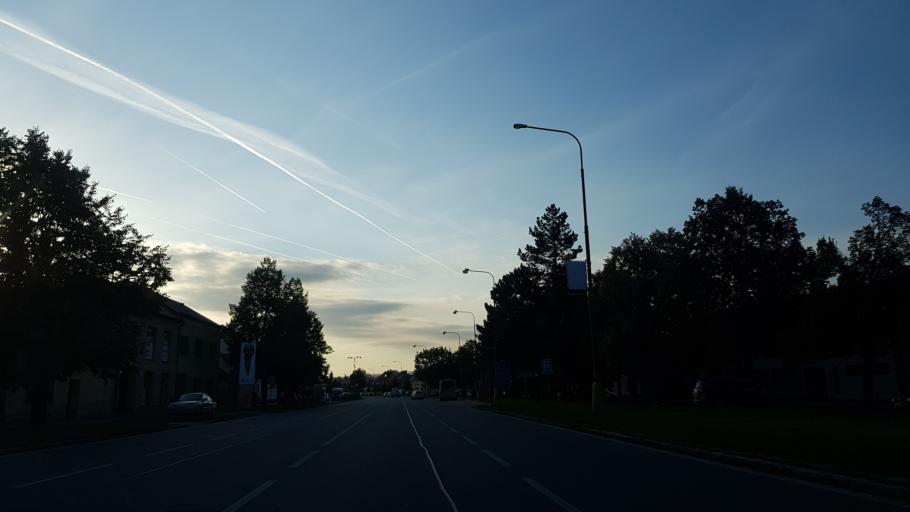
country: CZ
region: Zlin
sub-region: Okres Uherske Hradiste
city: Uherske Hradiste
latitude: 49.0756
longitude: 17.4507
